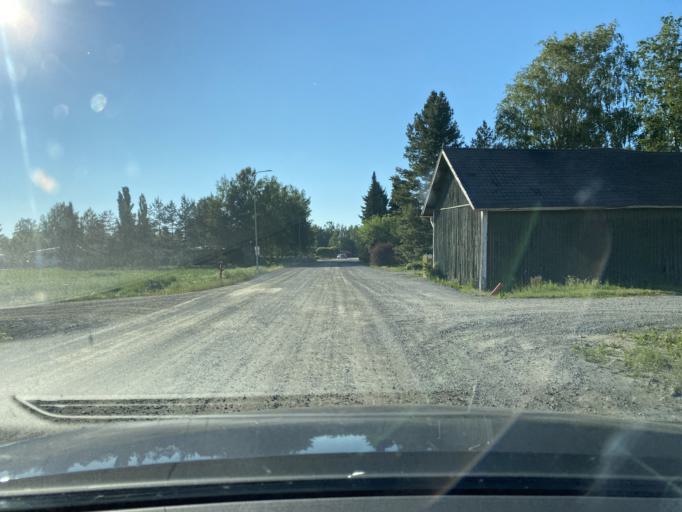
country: FI
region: Satakunta
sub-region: Pori
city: Huittinen
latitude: 61.1687
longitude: 22.7028
